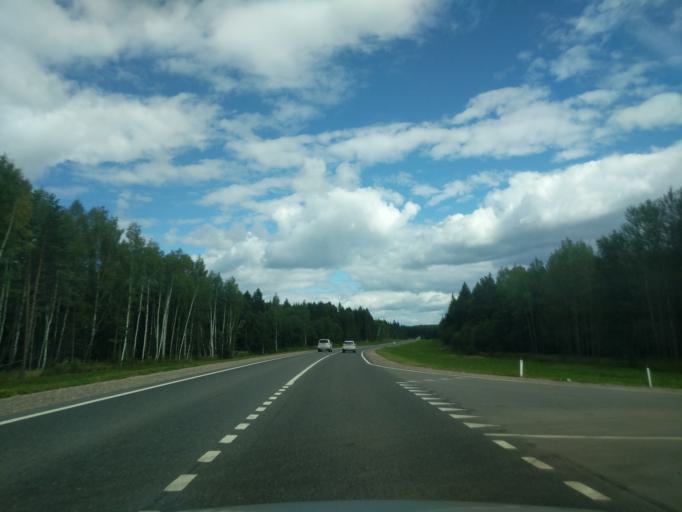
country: RU
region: Kostroma
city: Oktyabr'skiy
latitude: 57.7900
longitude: 41.1370
